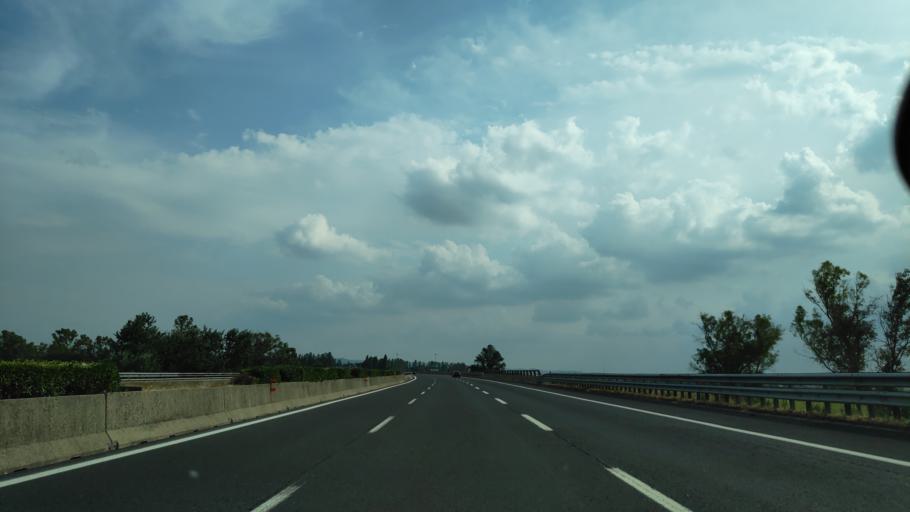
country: IT
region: Latium
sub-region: Citta metropolitana di Roma Capitale
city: Bivio di Capanelle
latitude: 42.1327
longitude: 12.6176
